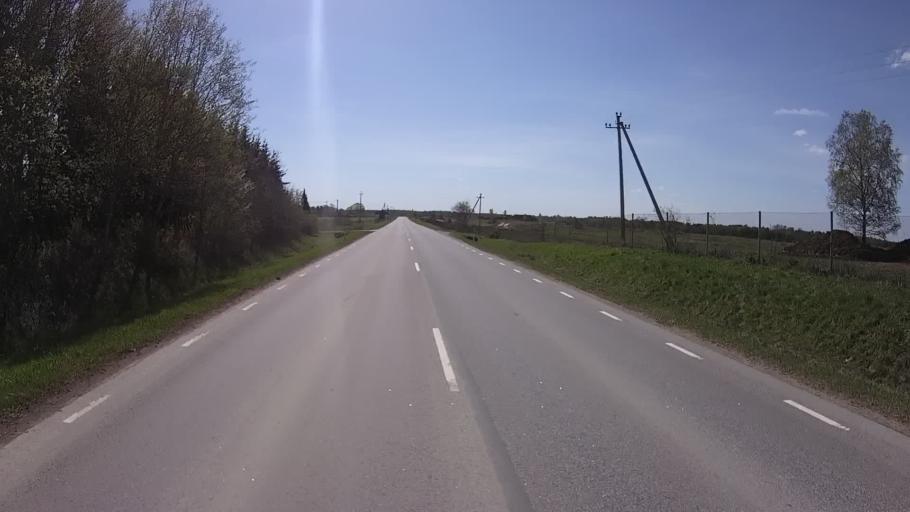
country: EE
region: Harju
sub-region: Keila linn
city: Keila
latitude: 59.3230
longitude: 24.3246
